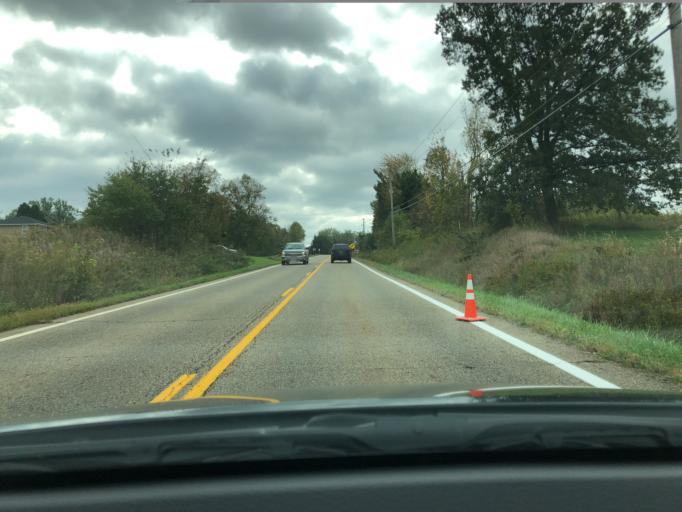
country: US
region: Ohio
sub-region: Stark County
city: Canal Fulton
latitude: 40.8482
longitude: -81.6027
